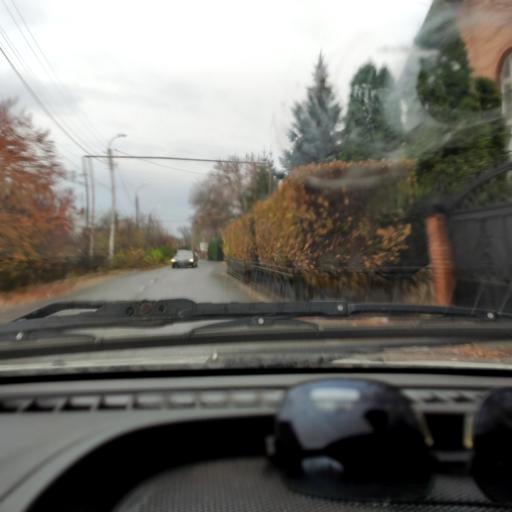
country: RU
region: Samara
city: Tol'yatti
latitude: 53.5346
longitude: 49.3881
